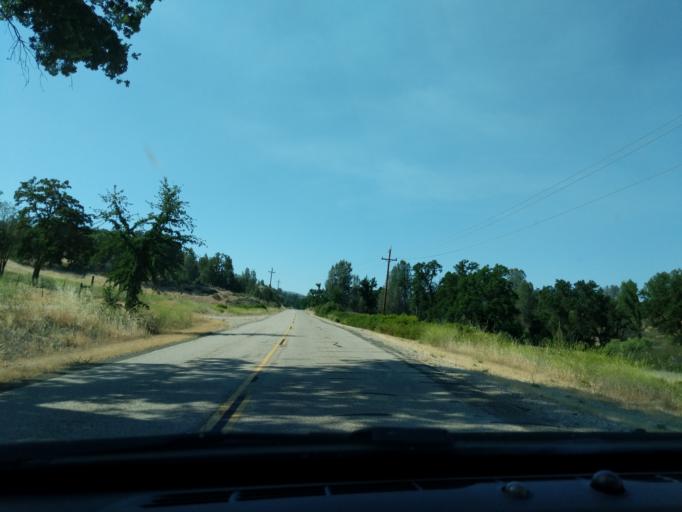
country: US
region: California
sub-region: Monterey County
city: King City
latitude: 35.9747
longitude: -121.1755
